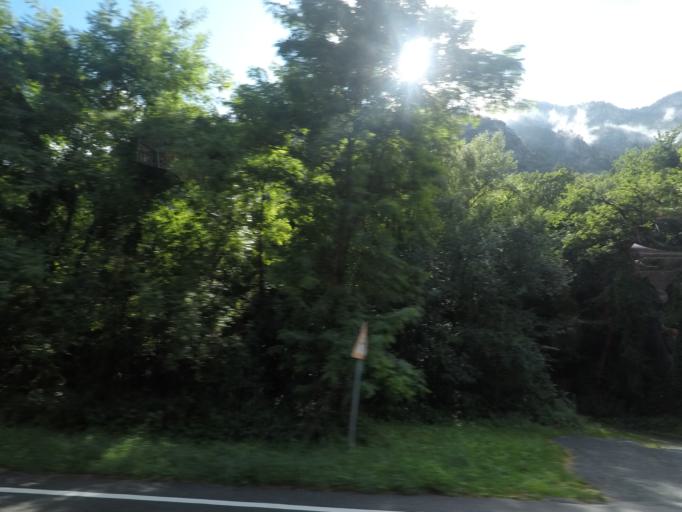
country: IT
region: Aosta Valley
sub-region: Valle d'Aosta
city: Chatillon
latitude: 45.7712
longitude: 7.5977
